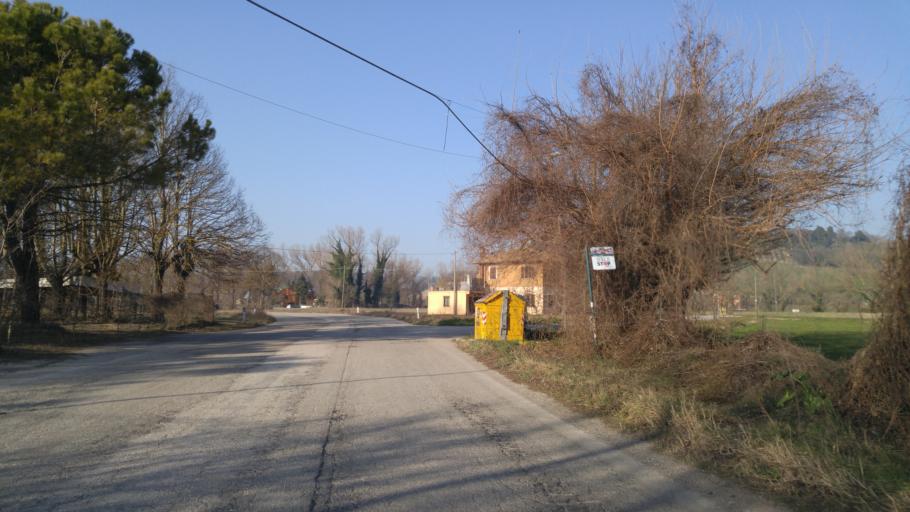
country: IT
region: The Marches
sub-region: Provincia di Pesaro e Urbino
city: Fenile
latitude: 43.8298
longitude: 12.9167
